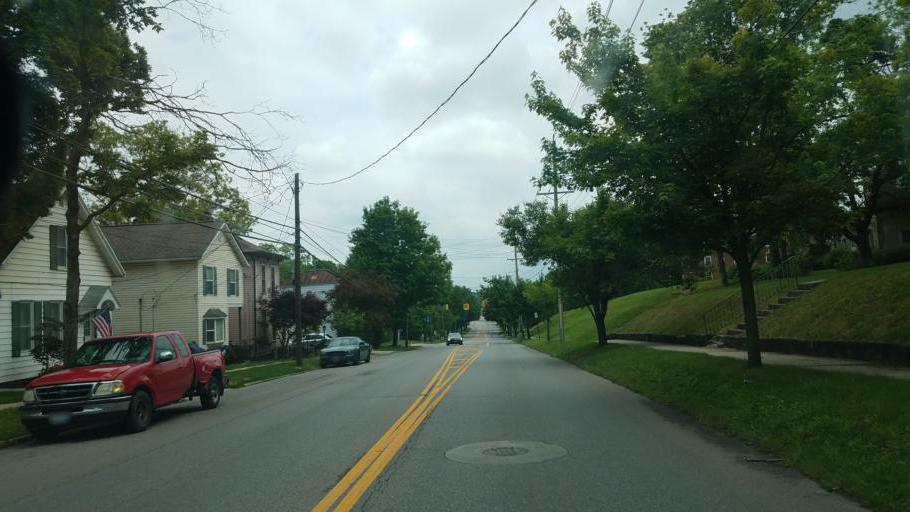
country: US
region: Ohio
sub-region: Delaware County
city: Delaware
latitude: 40.2993
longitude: -83.0774
